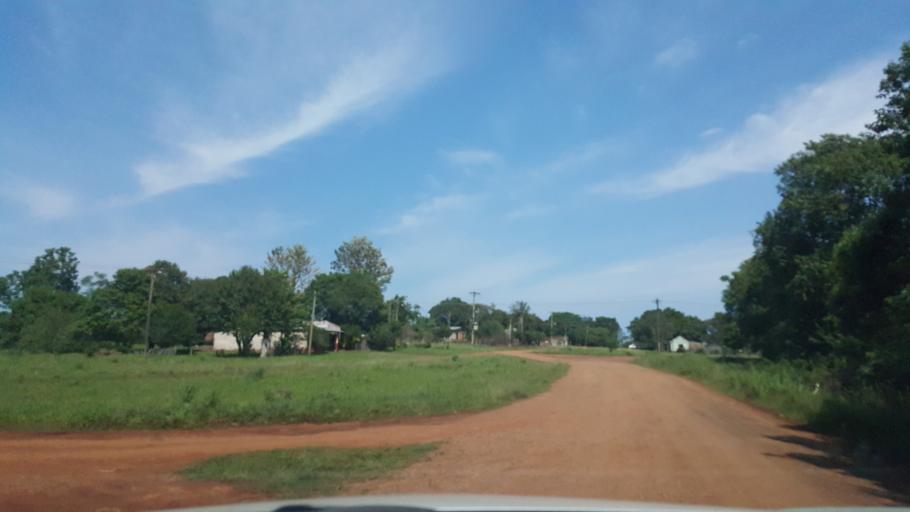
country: AR
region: Misiones
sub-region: Departamento de Apostoles
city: San Jose
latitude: -27.7483
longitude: -55.7916
